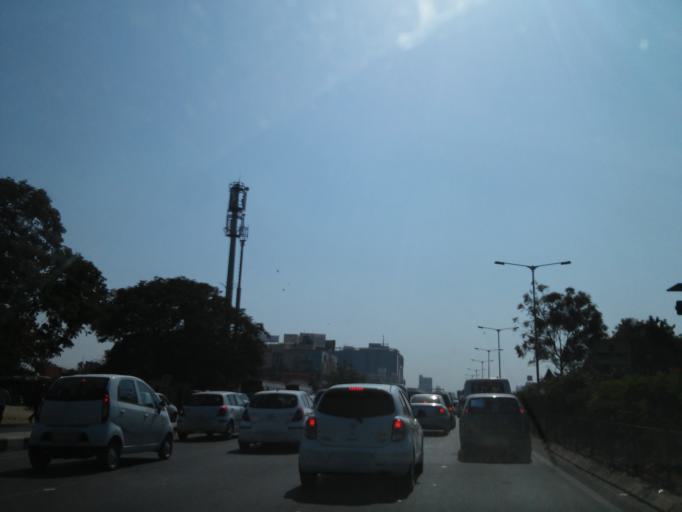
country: IN
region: Gujarat
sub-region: Ahmadabad
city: Ahmedabad
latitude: 23.0805
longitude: 72.5264
